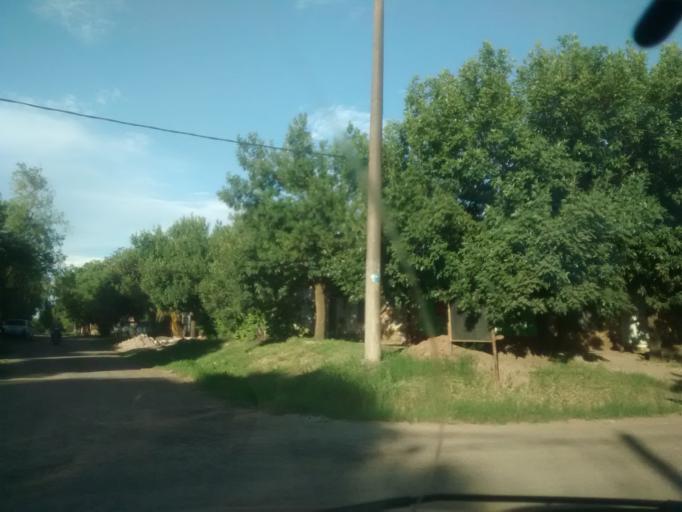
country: AR
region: Chaco
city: Resistencia
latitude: -27.4312
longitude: -58.9948
